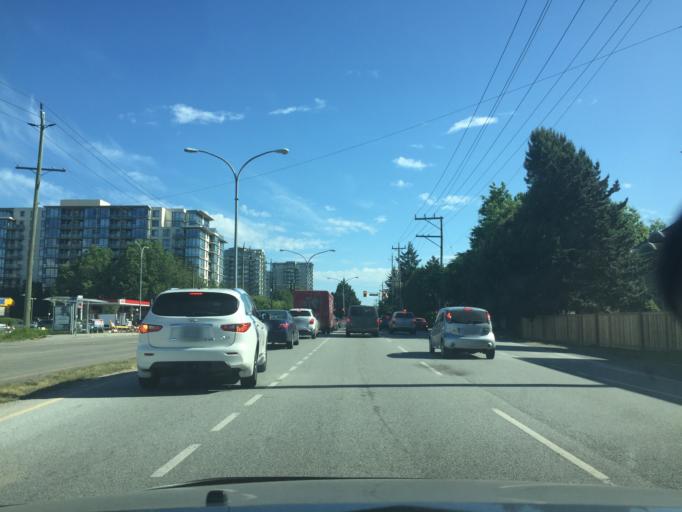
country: CA
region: British Columbia
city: Richmond
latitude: 49.1710
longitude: -123.1247
